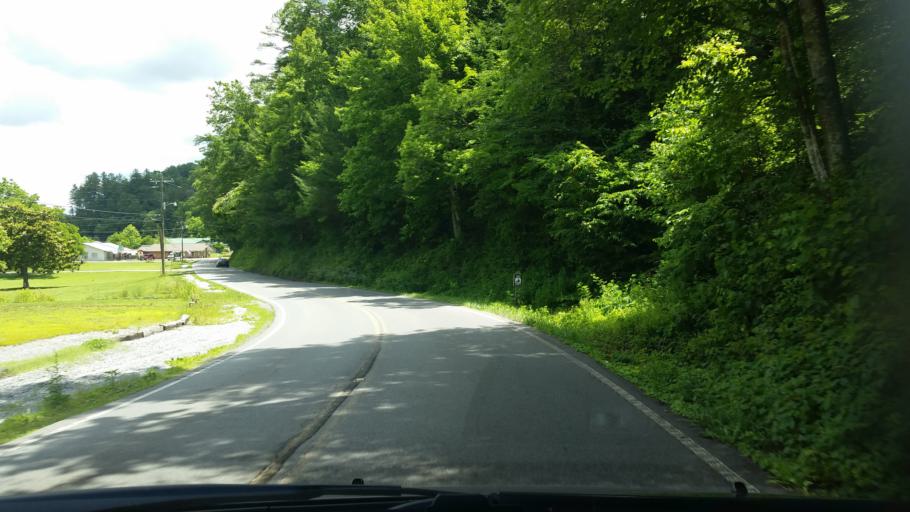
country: US
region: Tennessee
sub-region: Sevier County
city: Gatlinburg
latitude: 35.7448
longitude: -83.4532
